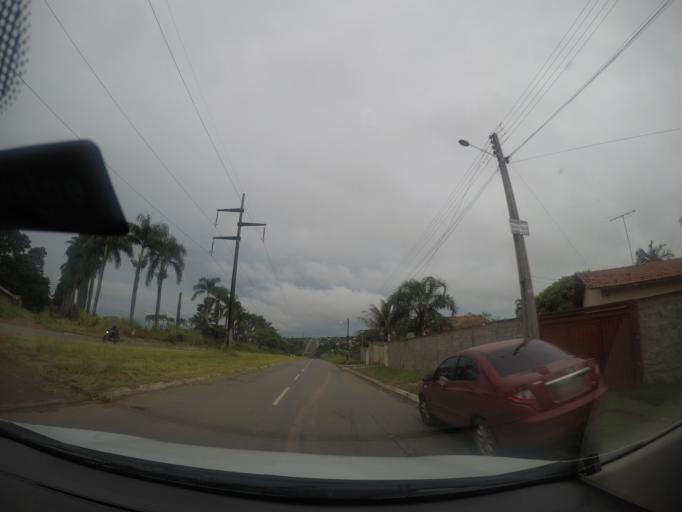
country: BR
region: Goias
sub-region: Aparecida De Goiania
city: Aparecida de Goiania
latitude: -16.7636
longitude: -49.3055
